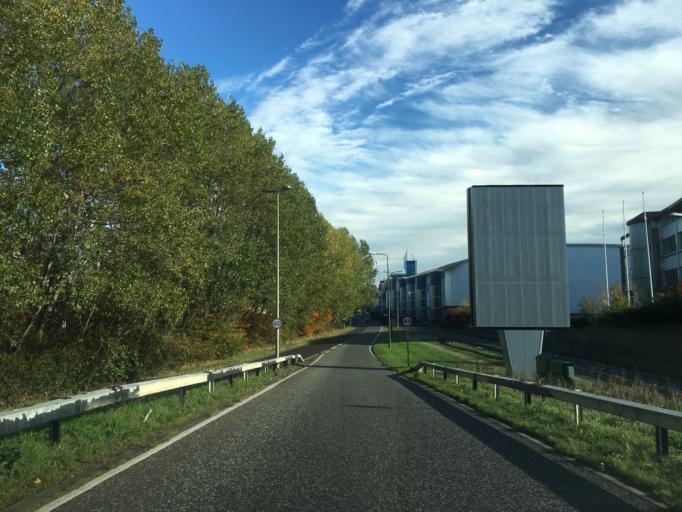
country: GB
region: Scotland
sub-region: Edinburgh
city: Edinburgh
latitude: 55.9404
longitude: -3.2212
